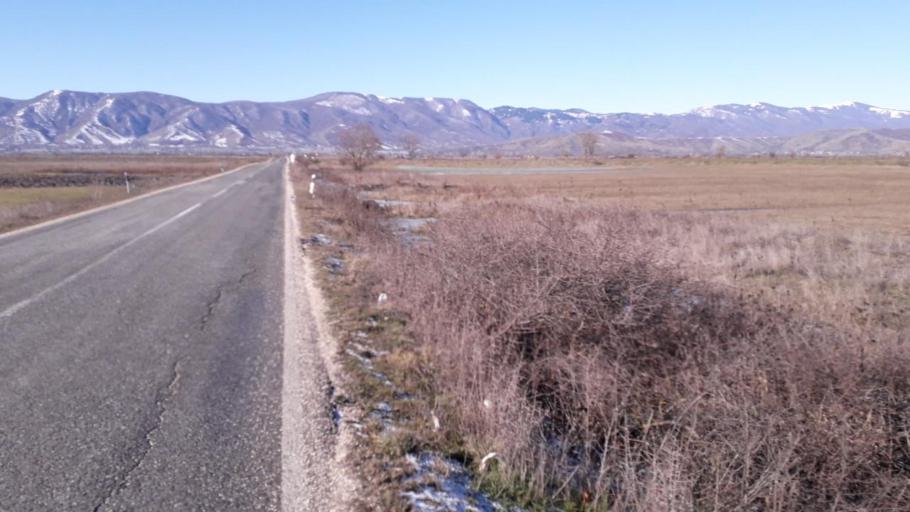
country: MK
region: Krivogastani
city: Krivogashtani
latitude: 41.3367
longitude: 21.3770
